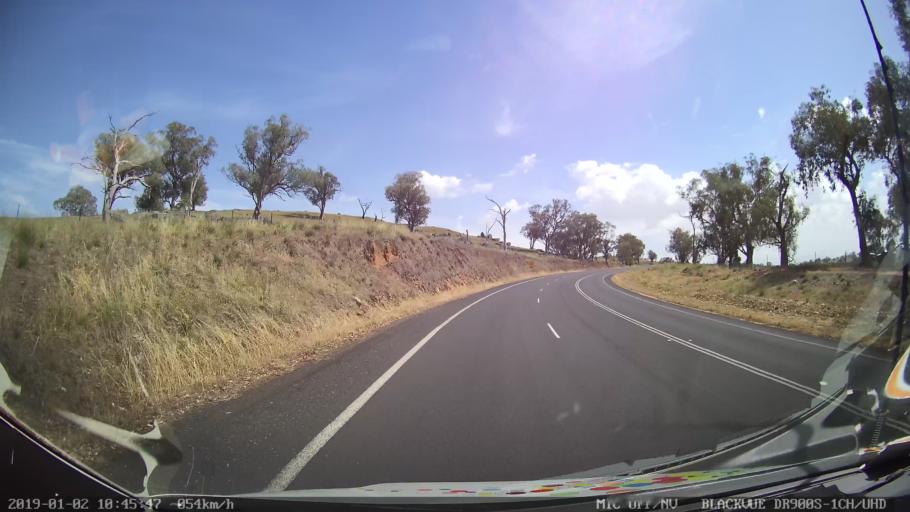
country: AU
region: New South Wales
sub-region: Cootamundra
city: Cootamundra
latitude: -34.7570
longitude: 148.2888
